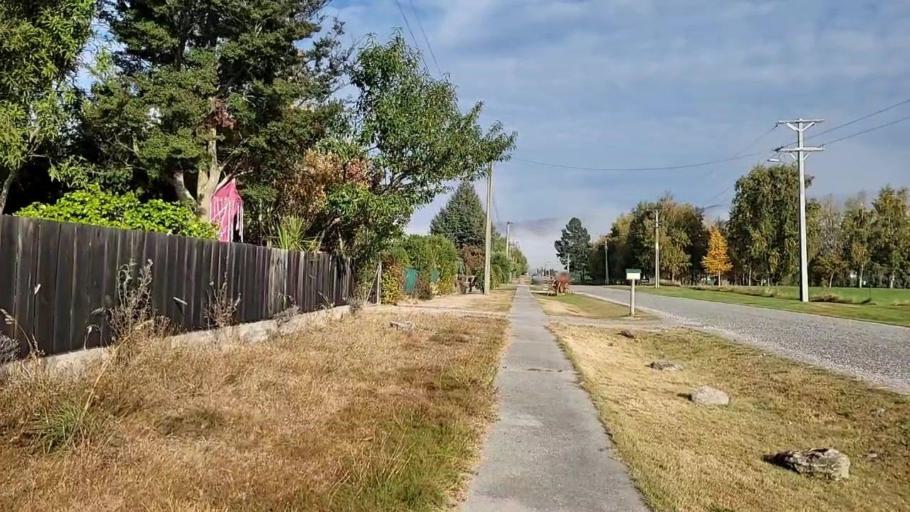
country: NZ
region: Southland
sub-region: Gore District
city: Gore
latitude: -45.6332
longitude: 169.3664
